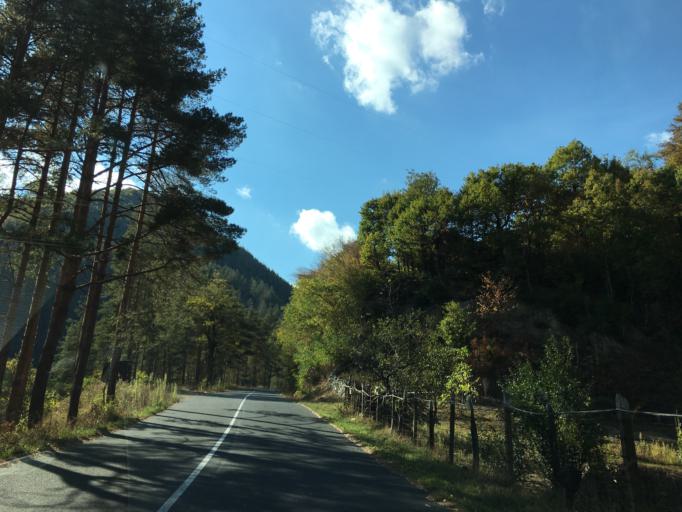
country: BG
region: Smolyan
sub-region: Obshtina Nedelino
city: Nedelino
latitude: 41.4362
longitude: 25.0253
